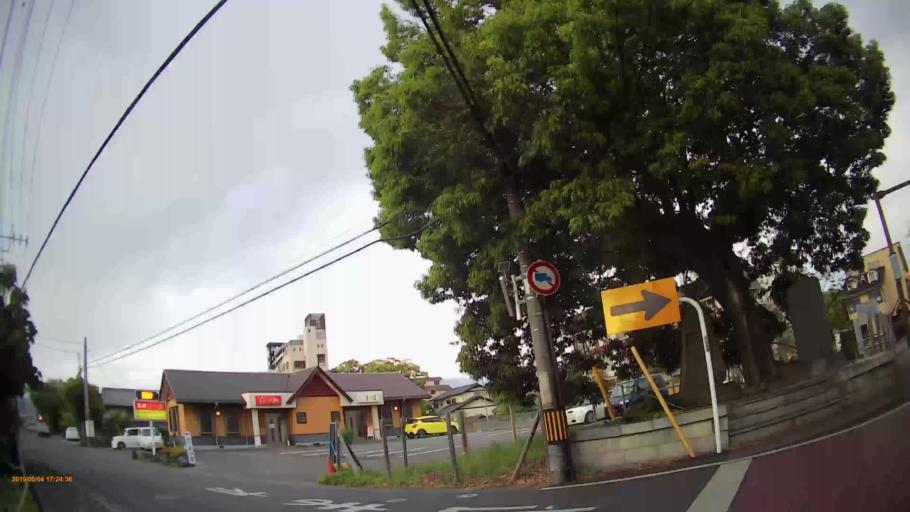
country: JP
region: Yamanashi
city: Isawa
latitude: 35.6517
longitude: 138.6326
